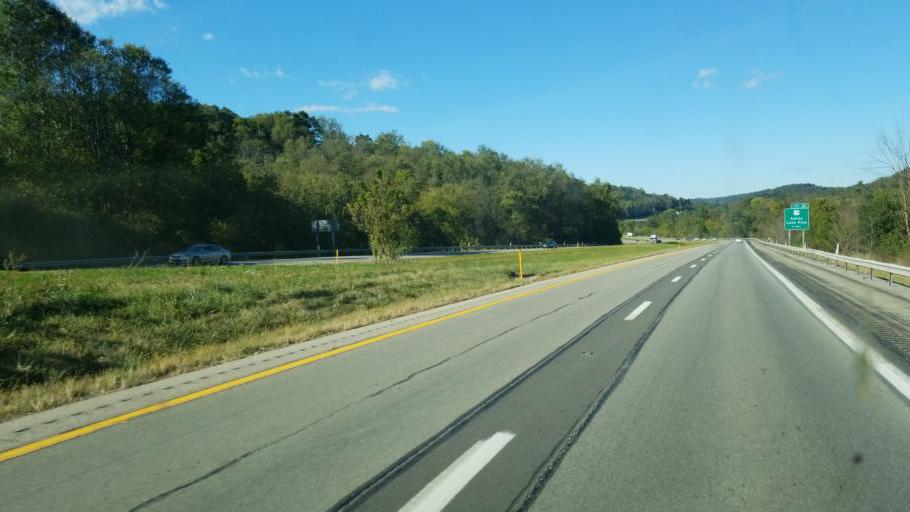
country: US
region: Pennsylvania
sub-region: Washington County
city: East Washington
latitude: 40.0919
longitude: -80.1931
